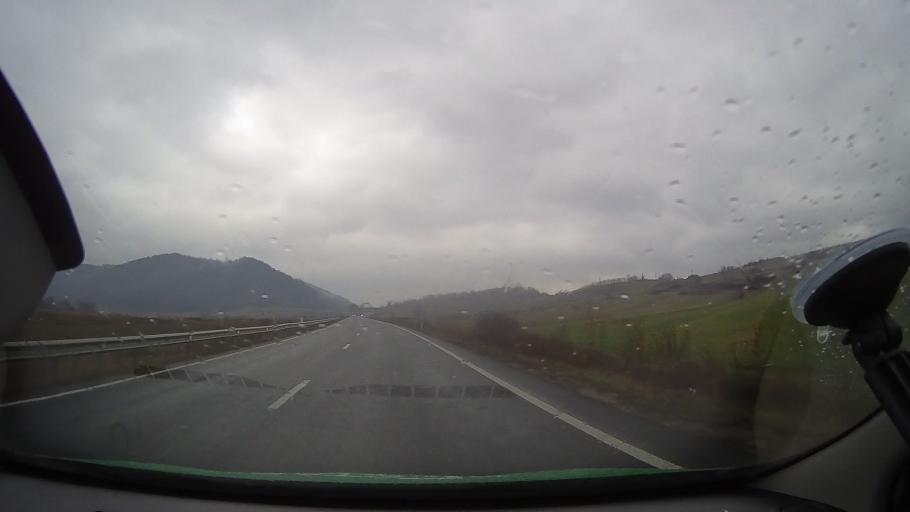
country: RO
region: Hunedoara
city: Vata de Jos
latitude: 46.1860
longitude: 22.6279
